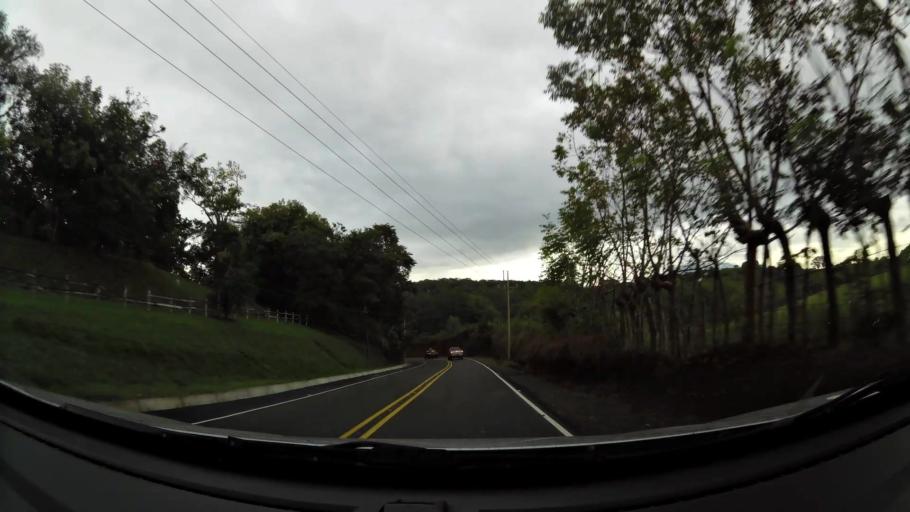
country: CR
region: Alajuela
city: Desamparados
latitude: 9.9389
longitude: -84.5339
